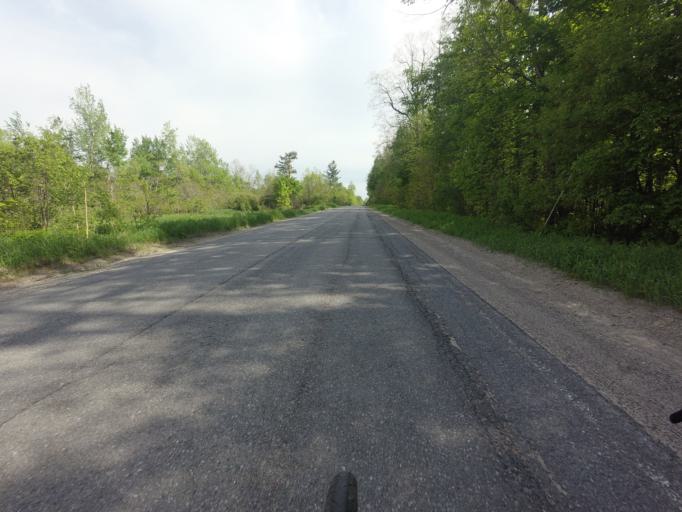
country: US
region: New York
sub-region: St. Lawrence County
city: Gouverneur
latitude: 44.2587
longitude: -75.2221
